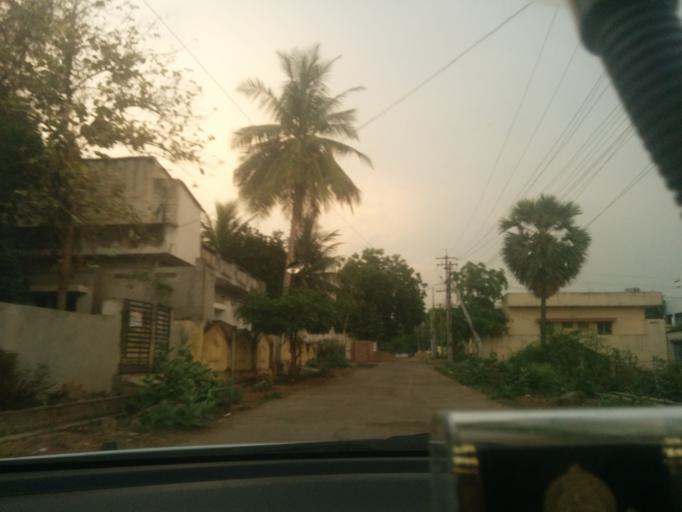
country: IN
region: Andhra Pradesh
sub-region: East Godavari
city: Rajahmundry
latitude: 17.0231
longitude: 81.7934
